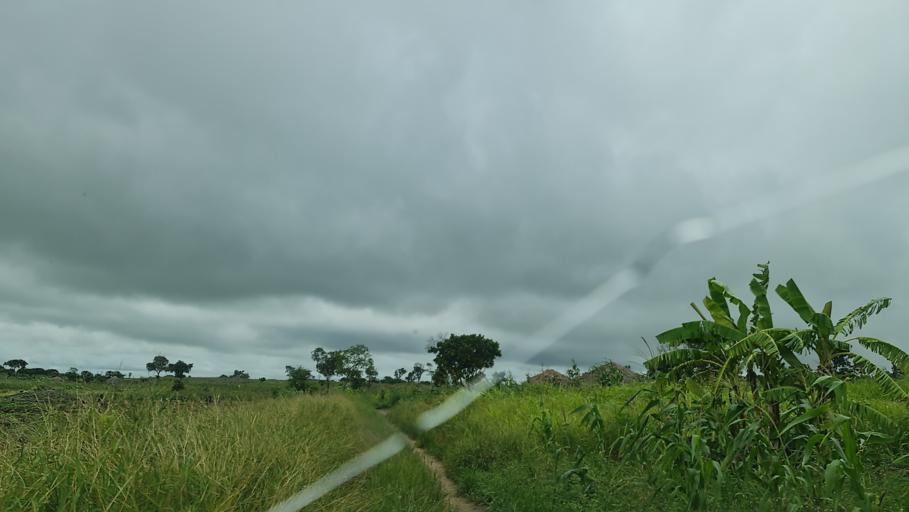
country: MW
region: Southern Region
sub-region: Nsanje District
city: Nsanje
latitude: -17.3401
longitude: 35.7287
